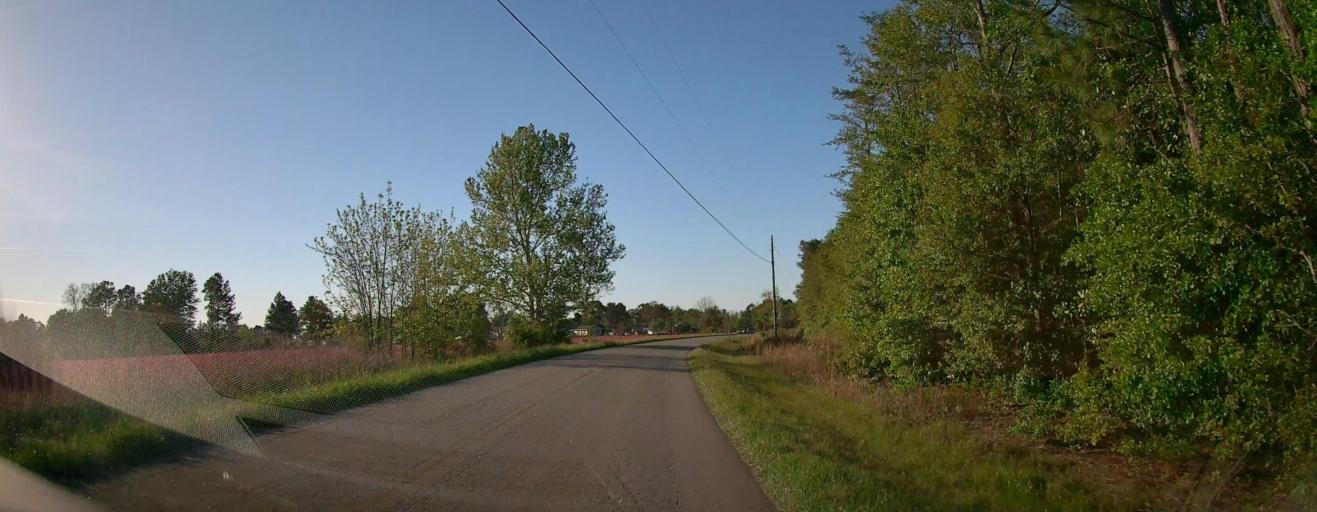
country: US
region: Georgia
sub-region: Ben Hill County
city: Fitzgerald
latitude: 31.6970
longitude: -83.2214
